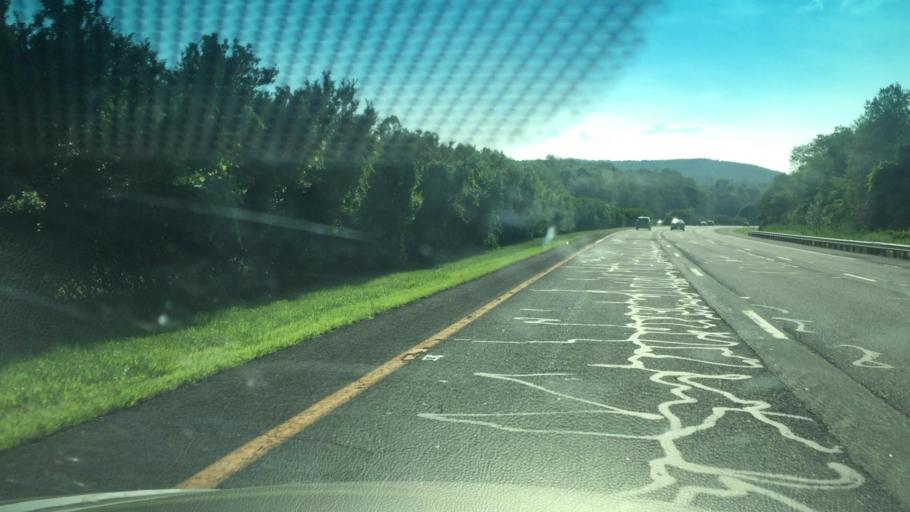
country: US
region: New Jersey
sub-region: Warren County
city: Hackettstown
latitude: 40.9231
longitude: -74.8704
